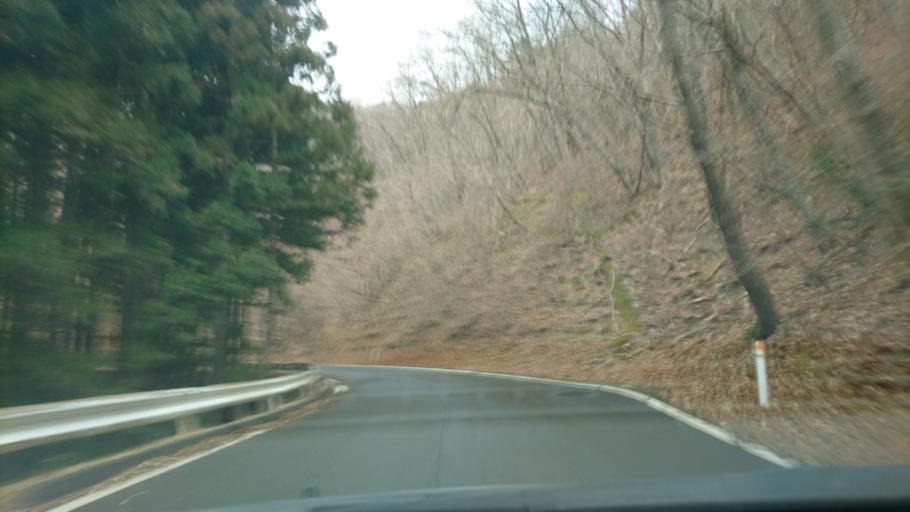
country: JP
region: Iwate
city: Ofunato
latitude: 38.9941
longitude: 141.5481
